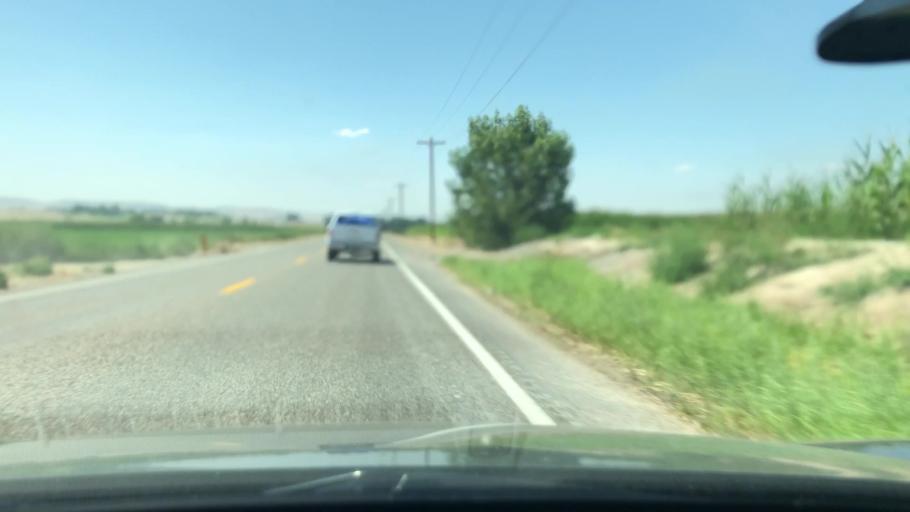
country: US
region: Idaho
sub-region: Owyhee County
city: Marsing
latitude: 43.5452
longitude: -116.8780
